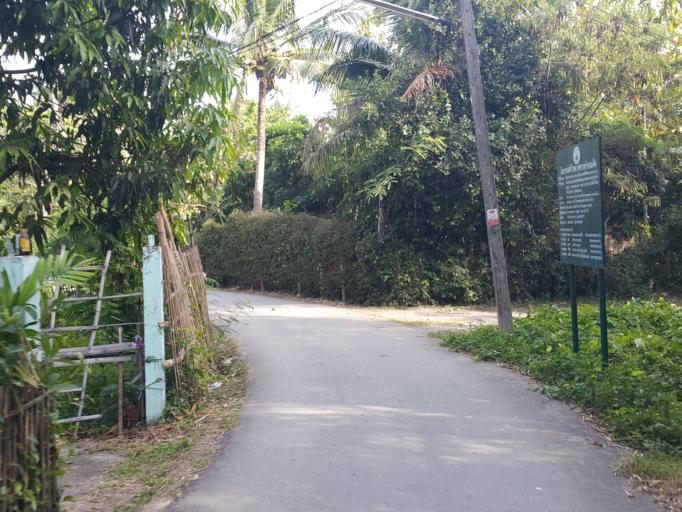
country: TH
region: Chiang Mai
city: San Kamphaeng
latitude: 18.7907
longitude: 99.1111
